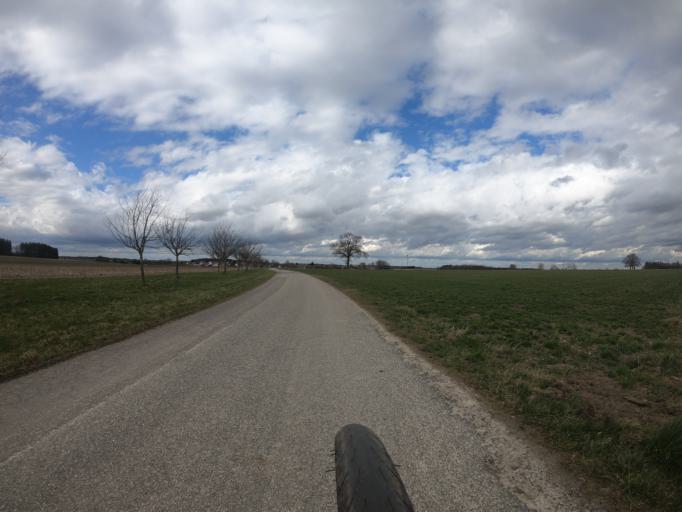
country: DE
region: Bavaria
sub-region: Upper Bavaria
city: Landsberied
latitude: 48.1730
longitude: 11.1964
